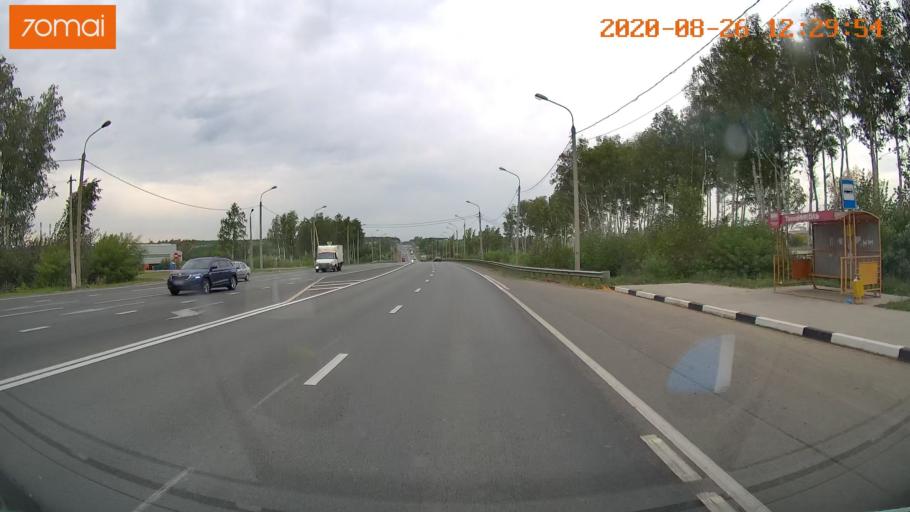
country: RU
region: Rjazan
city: Ryazan'
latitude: 54.5669
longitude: 39.8112
